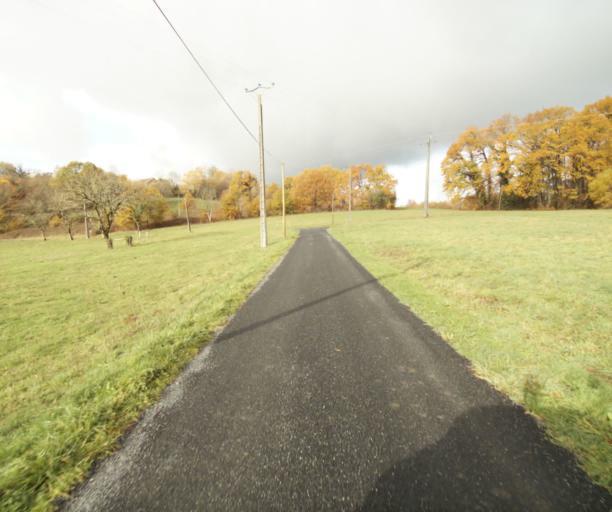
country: FR
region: Limousin
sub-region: Departement de la Correze
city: Sainte-Fereole
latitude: 45.2260
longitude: 1.6314
